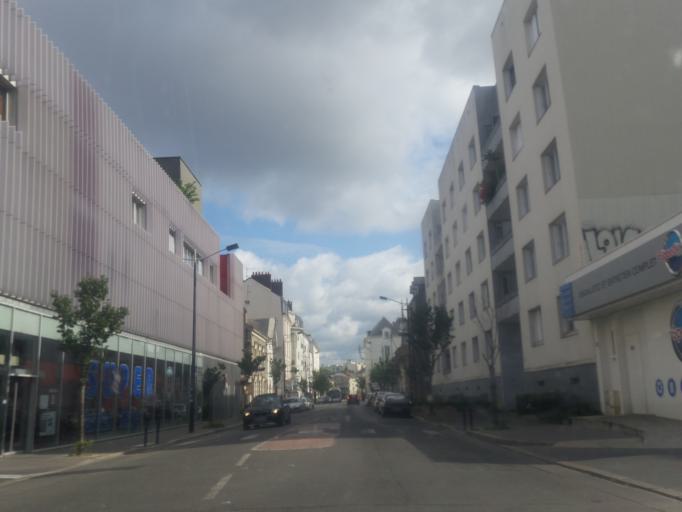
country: FR
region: Pays de la Loire
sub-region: Departement de la Loire-Atlantique
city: Nantes
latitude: 47.2239
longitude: -1.5299
